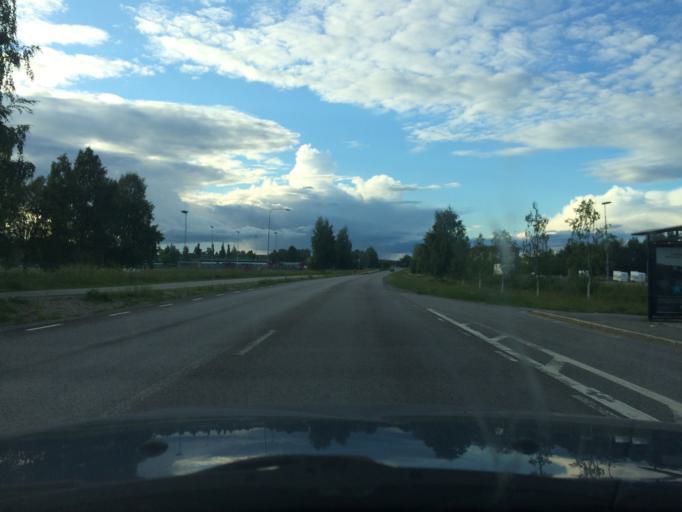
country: SE
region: Norrbotten
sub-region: Pitea Kommun
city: Bergsviken
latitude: 65.3411
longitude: 21.4067
